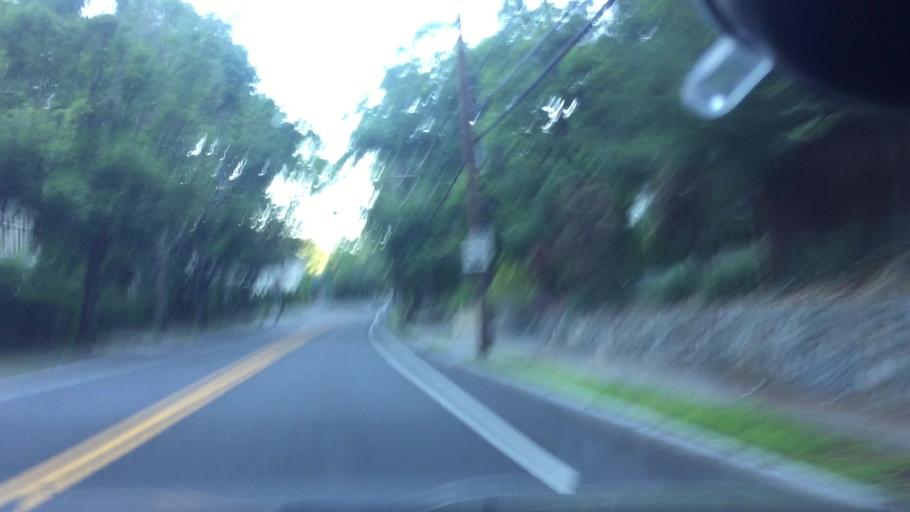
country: US
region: Massachusetts
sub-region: Middlesex County
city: Newton
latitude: 42.3092
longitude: -71.2074
